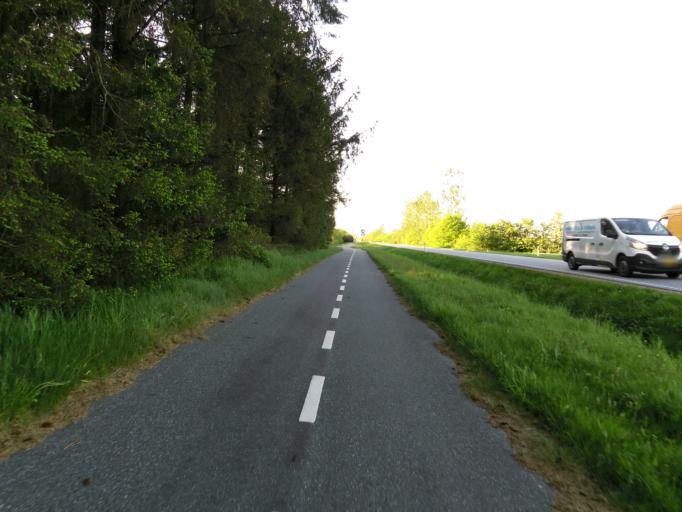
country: DK
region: South Denmark
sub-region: Esbjerg Kommune
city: Ribe
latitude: 55.2987
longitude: 8.7418
